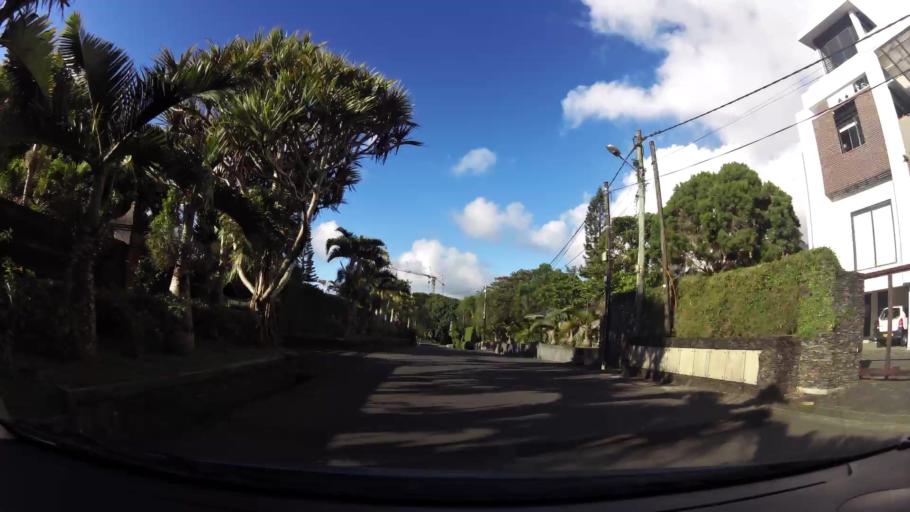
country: MU
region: Plaines Wilhems
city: Curepipe
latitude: -20.3103
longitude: 57.5113
